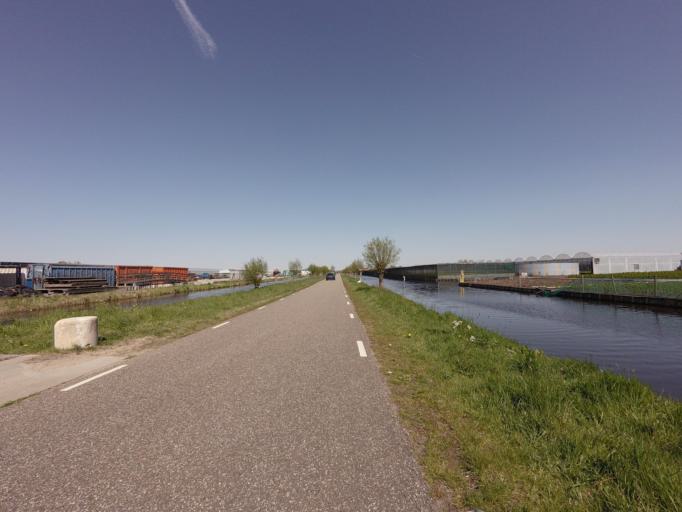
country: NL
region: South Holland
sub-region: Gemeente Boskoop
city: Boskoop
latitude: 52.0954
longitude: 4.6575
